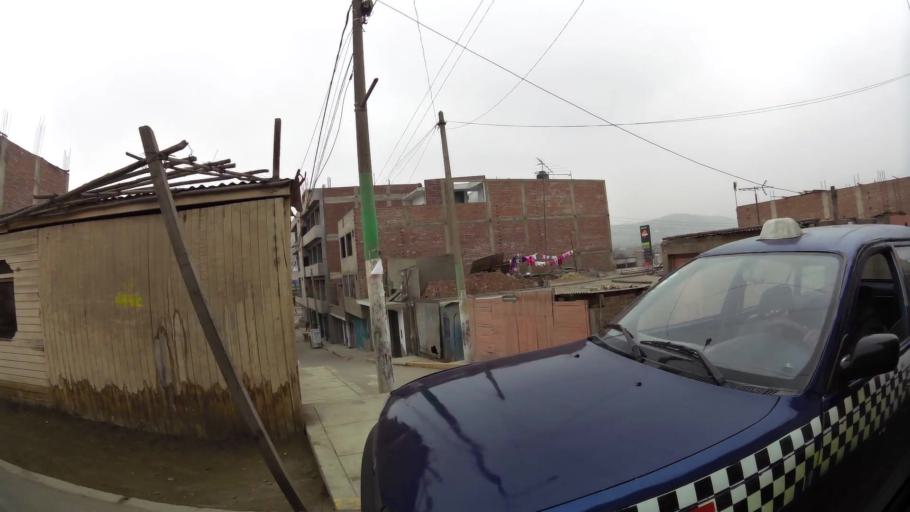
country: PE
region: Lima
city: Ventanilla
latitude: -11.8413
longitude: -77.1136
